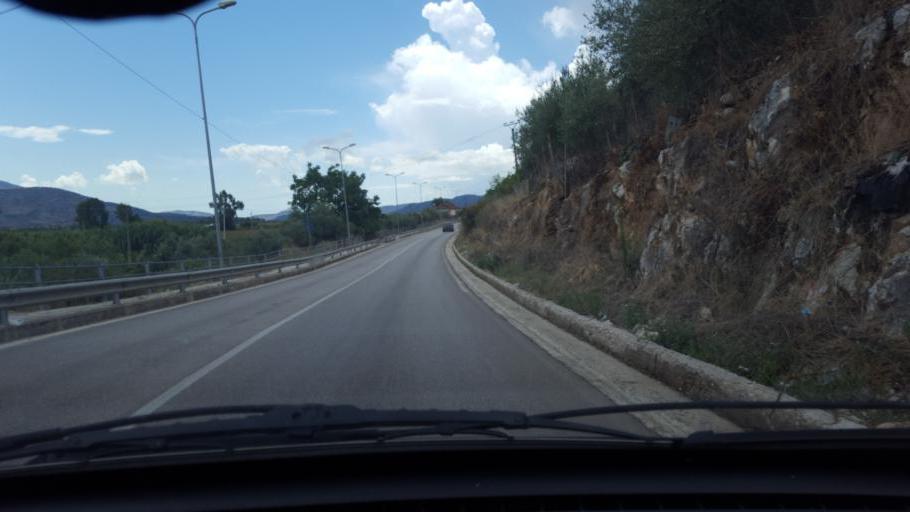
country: AL
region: Vlore
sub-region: Rrethi i Sarandes
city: Sarande
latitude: 39.8376
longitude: 20.0241
